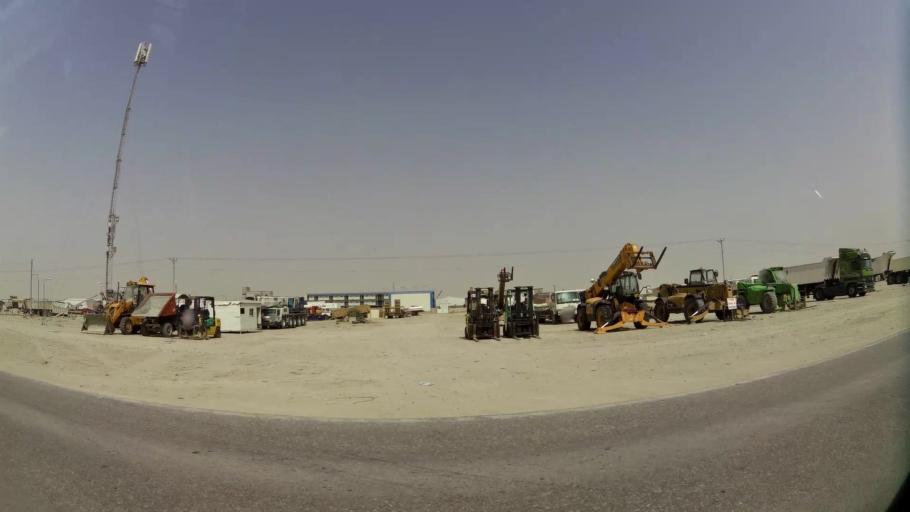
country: QA
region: Baladiyat ar Rayyan
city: Ar Rayyan
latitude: 25.2126
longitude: 51.3577
